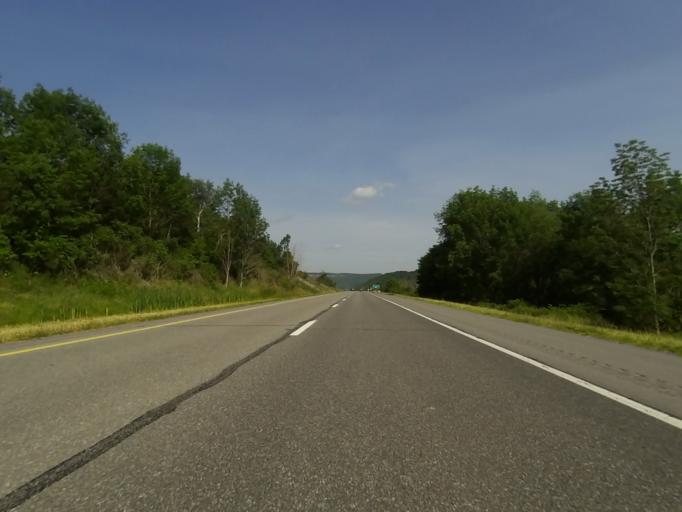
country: US
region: Pennsylvania
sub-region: Centre County
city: Stormstown
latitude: 40.8148
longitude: -78.0866
